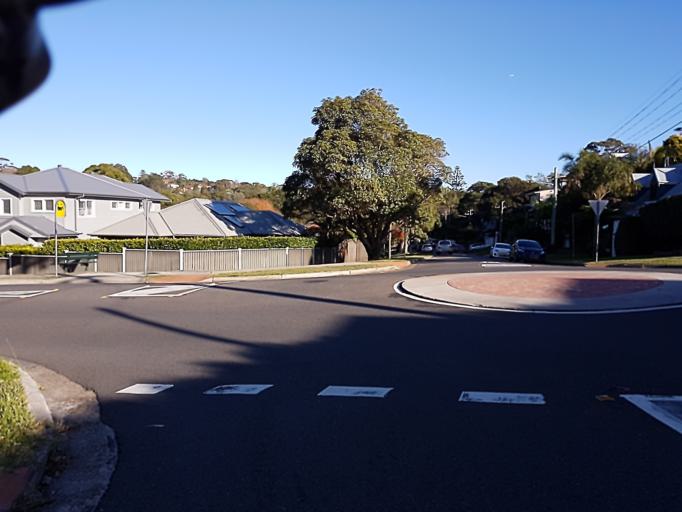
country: AU
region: New South Wales
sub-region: Manly Vale
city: Balgowlah
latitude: -33.7904
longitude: 151.2513
